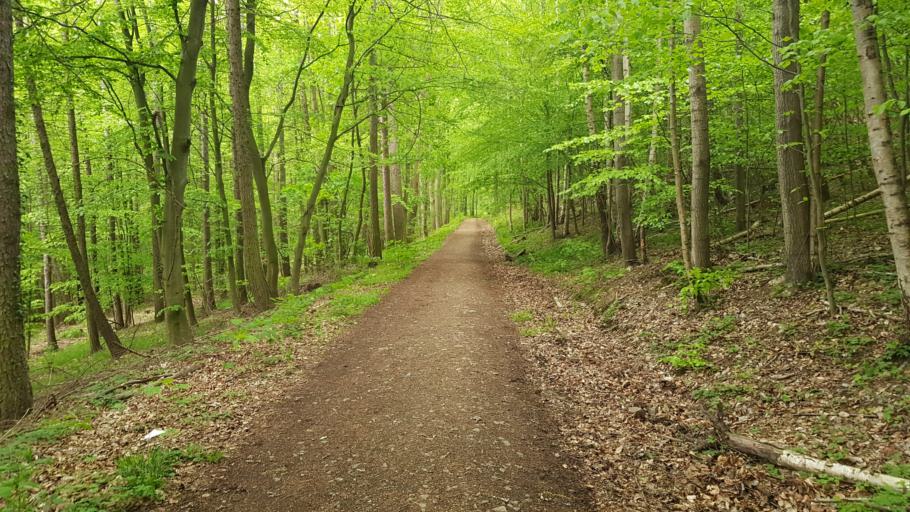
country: DE
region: Saxony-Anhalt
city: Neinstedt
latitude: 51.7392
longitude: 11.0677
